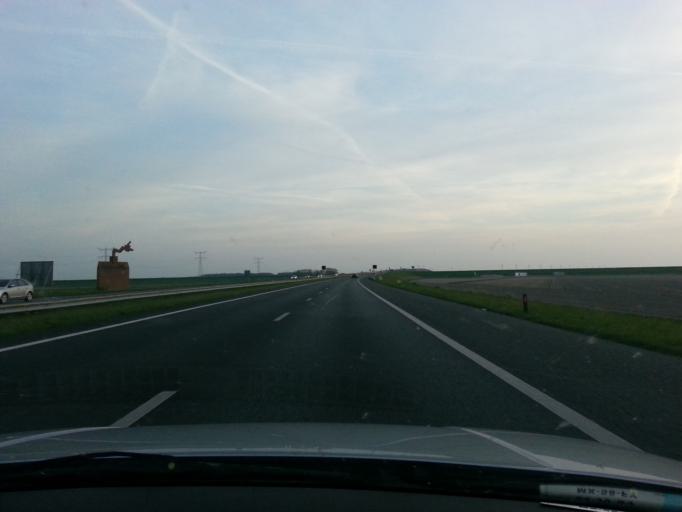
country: NL
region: Flevoland
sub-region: Gemeente Urk
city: Urk
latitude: 52.6216
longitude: 5.6610
